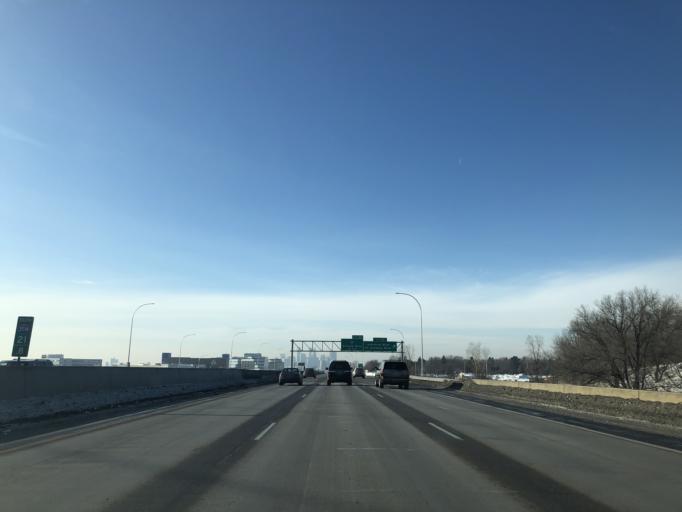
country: US
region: Minnesota
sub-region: Ramsey County
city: Lauderdale
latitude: 45.0069
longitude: -93.2069
